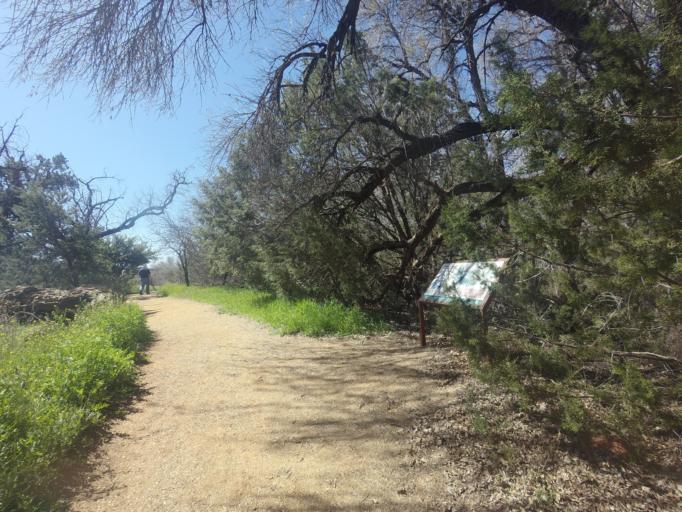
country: US
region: Arizona
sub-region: Yavapai County
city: Lake Montezuma
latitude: 34.6647
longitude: -111.7180
